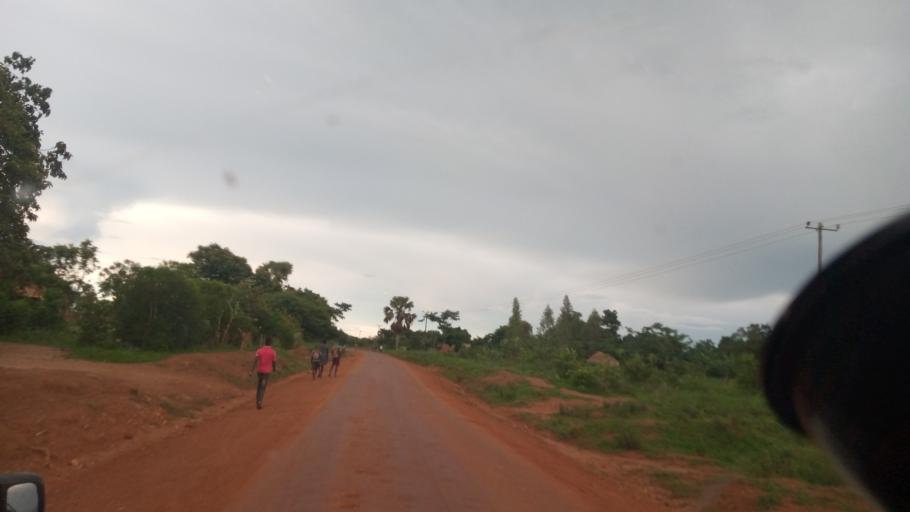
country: UG
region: Northern Region
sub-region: Kole District
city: Kole
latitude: 2.4686
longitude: 32.9364
